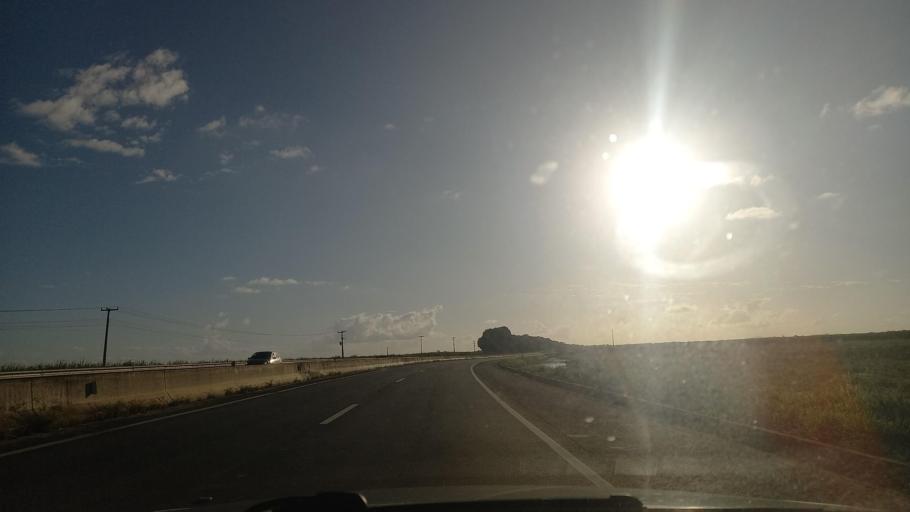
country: BR
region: Alagoas
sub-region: Campo Alegre
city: Campo Alegre
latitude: -9.8008
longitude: -36.2848
